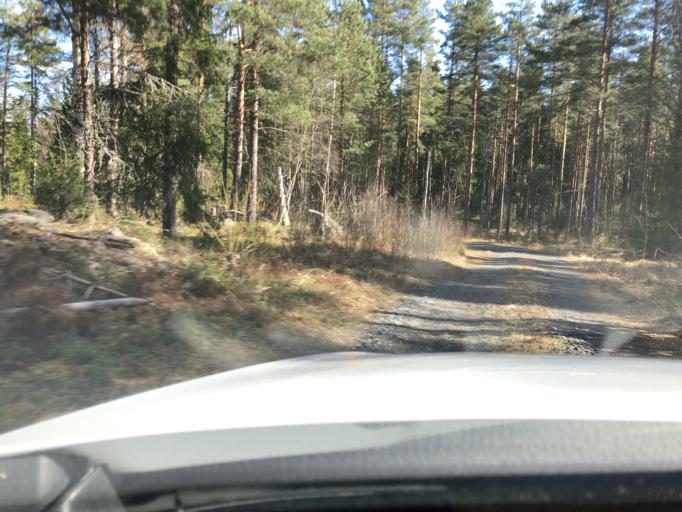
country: SE
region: Uppsala
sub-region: Heby Kommun
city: OEstervala
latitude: 60.3297
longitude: 17.1759
